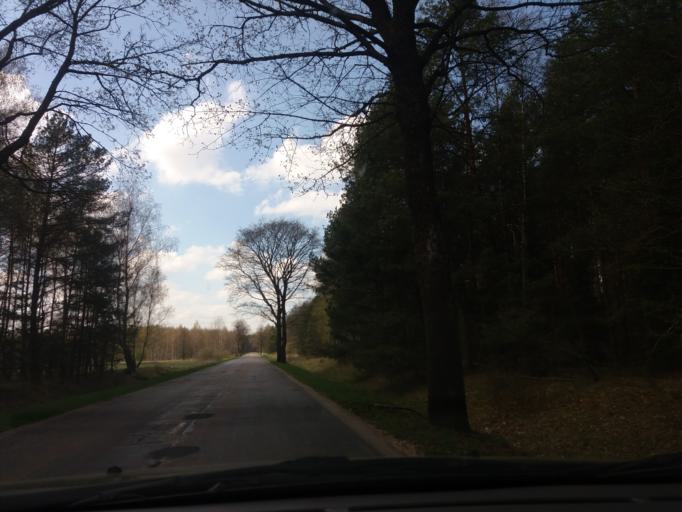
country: PL
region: Warmian-Masurian Voivodeship
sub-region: Powiat szczycienski
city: Jedwabno
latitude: 53.3612
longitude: 20.6931
